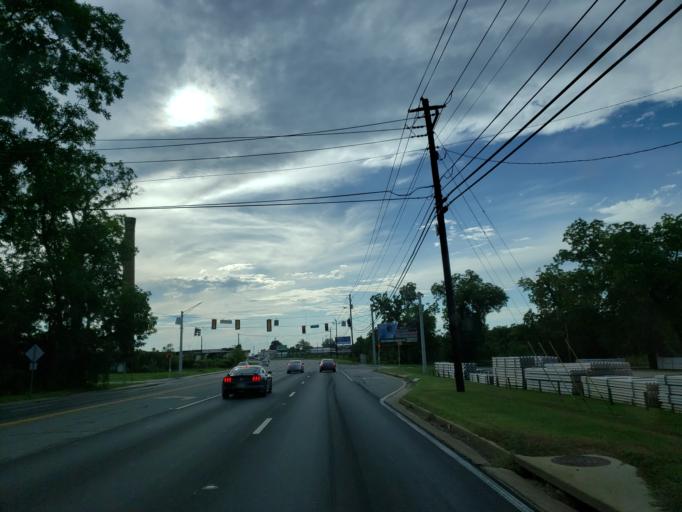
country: US
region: Georgia
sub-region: Tift County
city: Tifton
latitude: 31.4494
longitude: -83.4953
